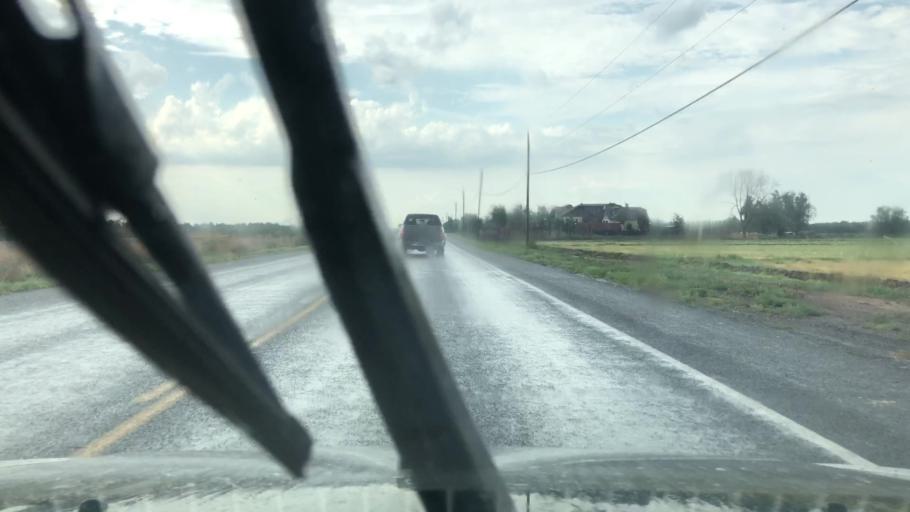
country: US
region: New Mexico
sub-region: Dona Ana County
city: Mesquite
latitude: 32.1858
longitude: -106.7099
